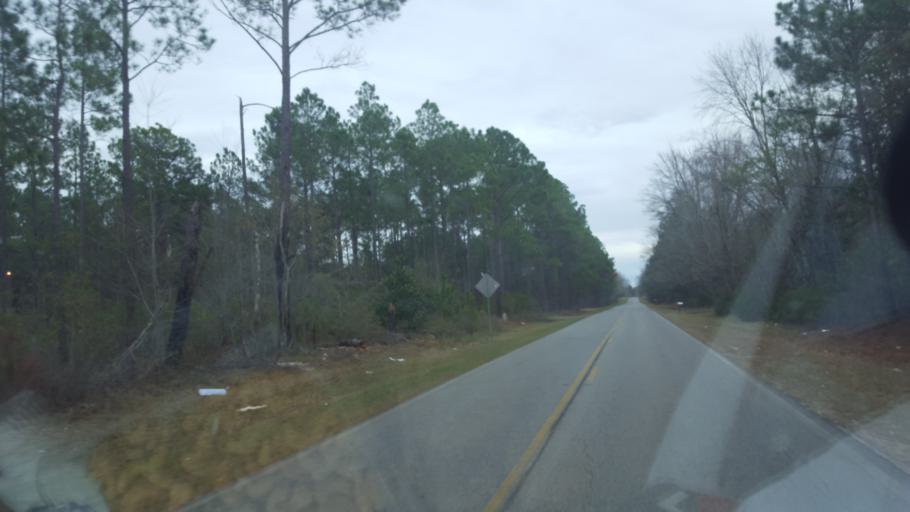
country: US
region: Georgia
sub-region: Ben Hill County
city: Fitzgerald
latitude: 31.7518
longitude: -83.3362
